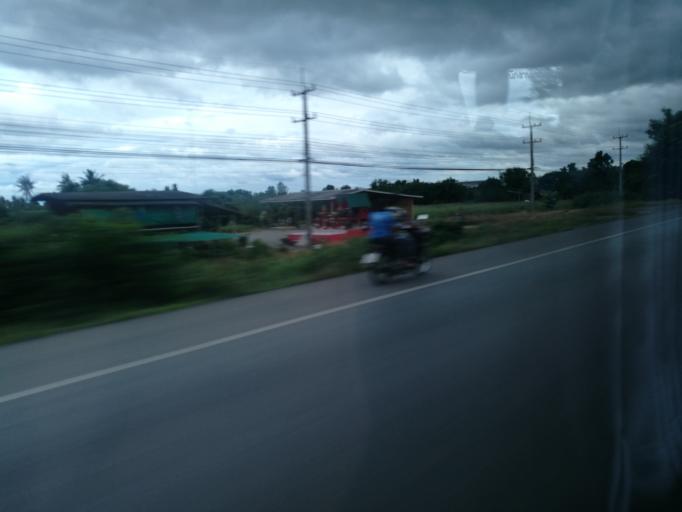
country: TH
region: Prachuap Khiri Khan
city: Sam Roi Yot
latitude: 12.1907
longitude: 99.8521
